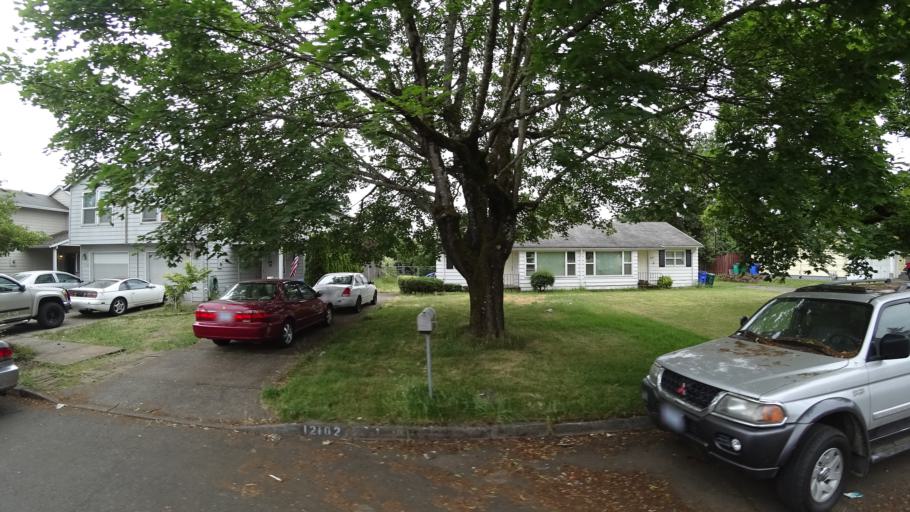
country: US
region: Oregon
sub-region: Multnomah County
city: Lents
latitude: 45.5008
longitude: -122.5386
